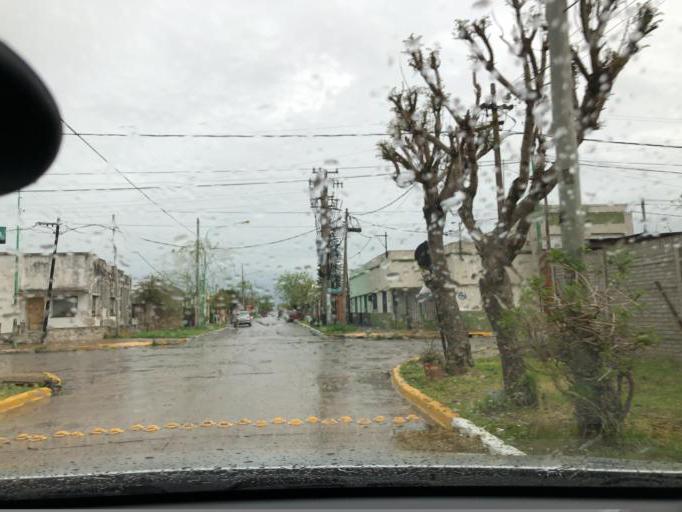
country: AR
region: Buenos Aires
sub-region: Partido de Ensenada
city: Ensenada
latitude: -34.8500
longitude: -57.9210
